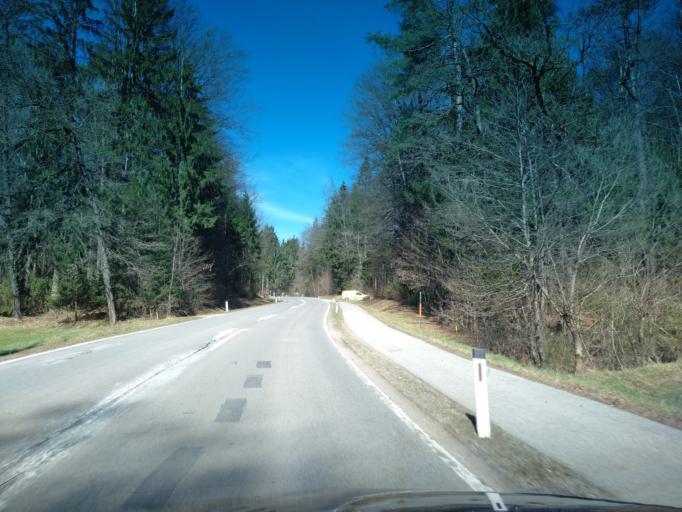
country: AT
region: Styria
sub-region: Politischer Bezirk Deutschlandsberg
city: Sankt Peter im Sulmtal
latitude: 46.7736
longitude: 15.2552
